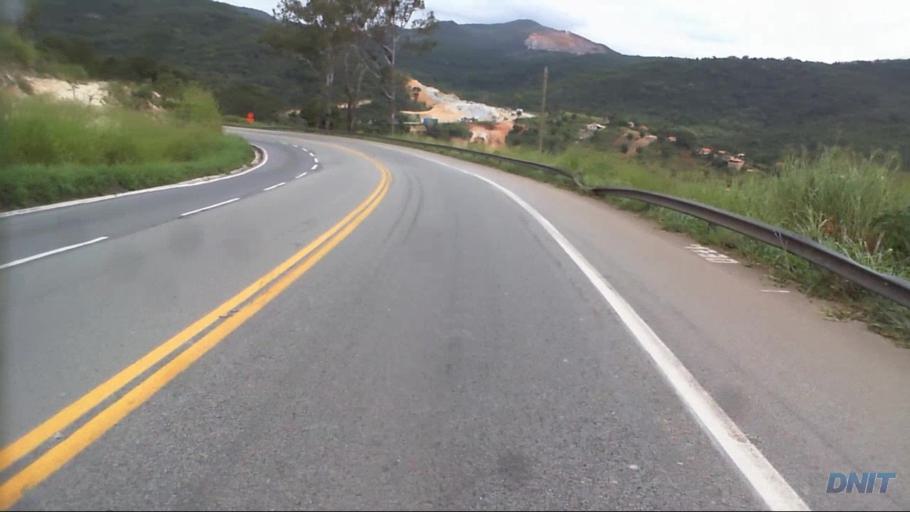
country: BR
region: Minas Gerais
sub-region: Caete
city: Caete
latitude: -19.7810
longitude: -43.6601
